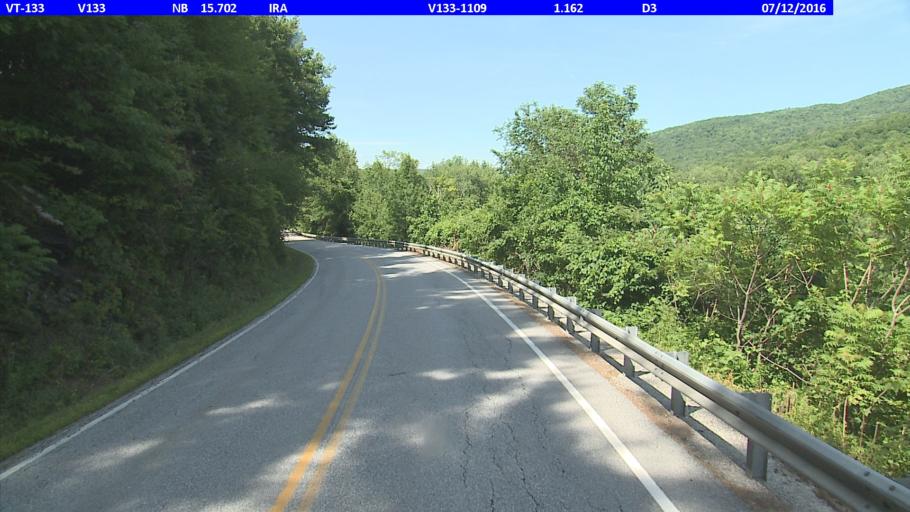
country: US
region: Vermont
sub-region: Rutland County
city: West Rutland
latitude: 43.5105
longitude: -73.0736
